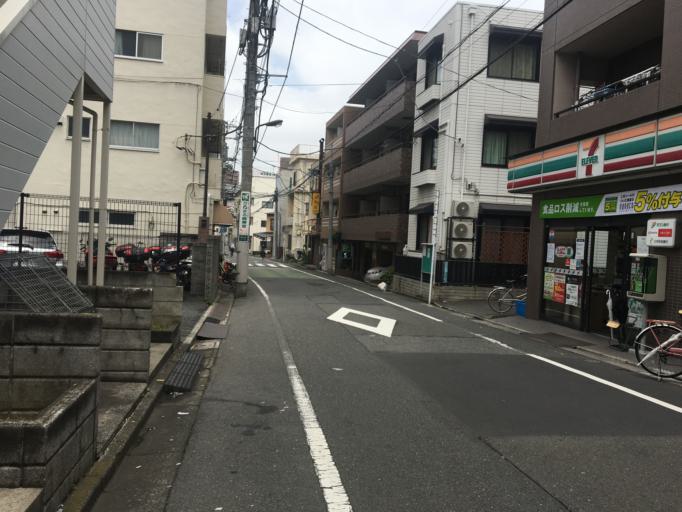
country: JP
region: Tokyo
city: Tokyo
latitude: 35.7439
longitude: 139.7102
